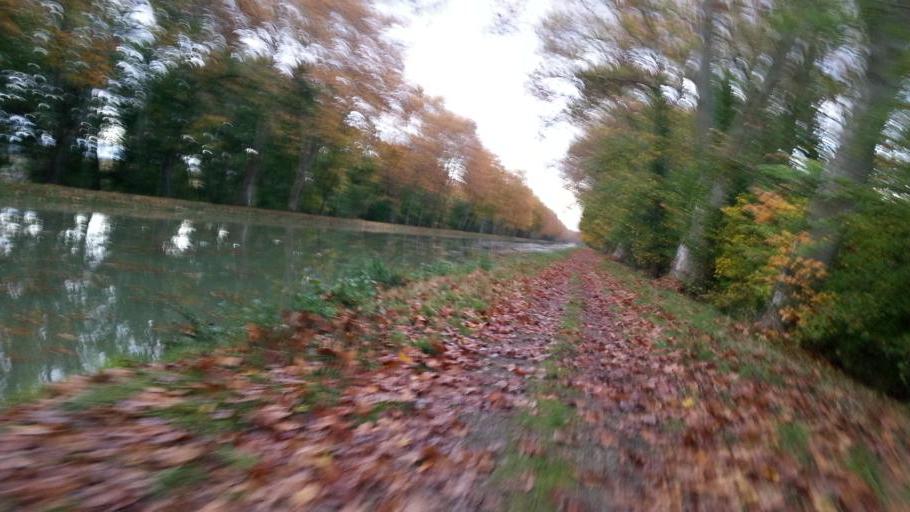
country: FR
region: Midi-Pyrenees
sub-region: Departement du Tarn-et-Garonne
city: Moissac
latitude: 44.0794
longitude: 1.0996
